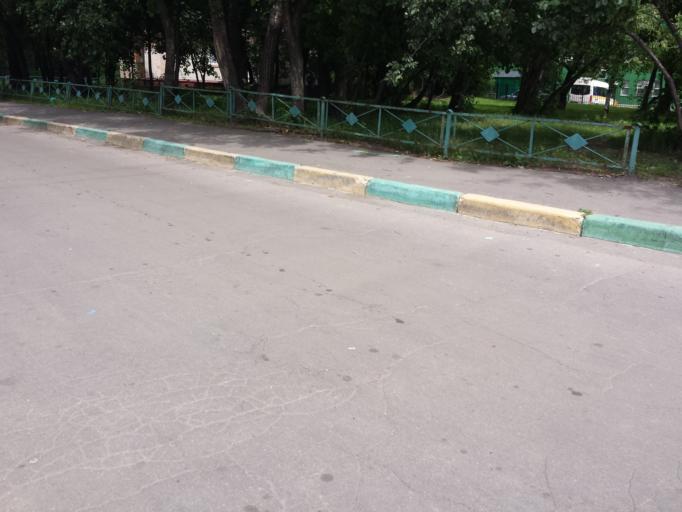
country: RU
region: Moskovskaya
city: Novogireyevo
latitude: 55.7462
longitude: 37.8250
